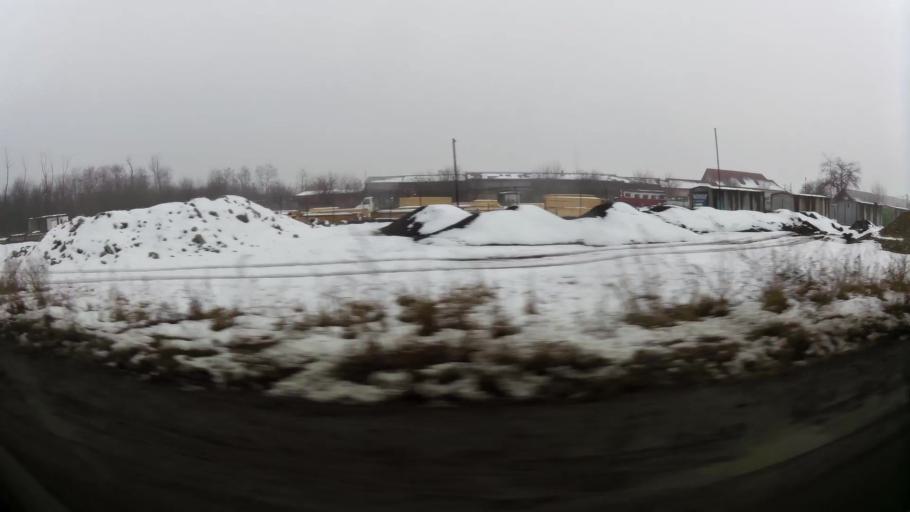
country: RO
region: Ilfov
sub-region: Comuna Clinceni
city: Olteni
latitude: 44.4054
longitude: 25.9766
